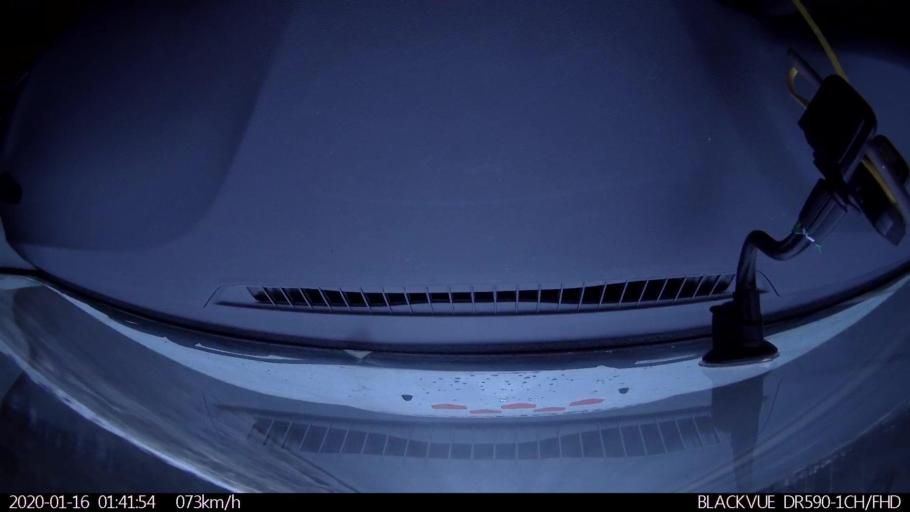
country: RU
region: Nizjnij Novgorod
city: Gorbatovka
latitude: 56.3175
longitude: 43.7591
